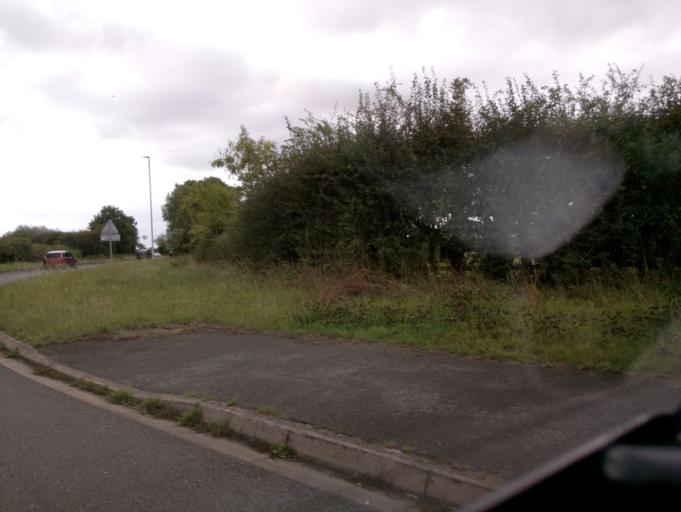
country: GB
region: England
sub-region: Devon
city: Exminster
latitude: 50.6750
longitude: -3.4866
